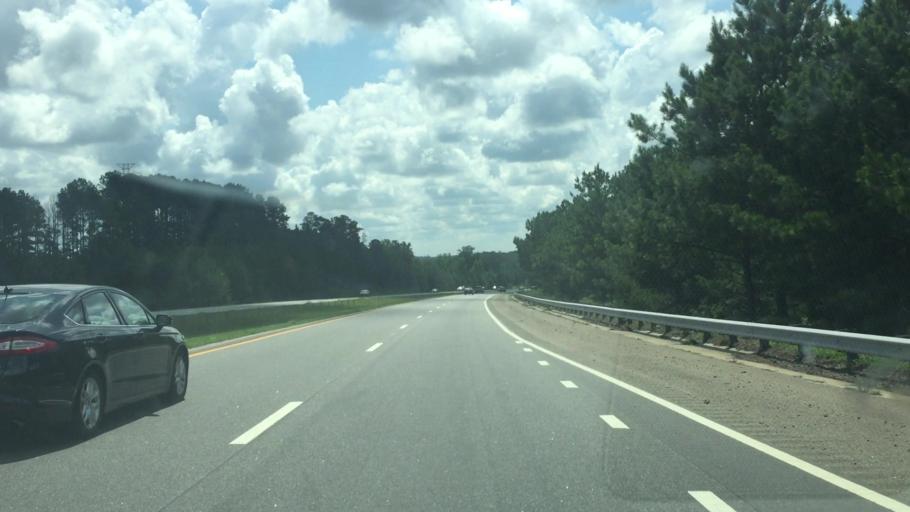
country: US
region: North Carolina
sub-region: Richmond County
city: Cordova
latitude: 34.9289
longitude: -79.8243
